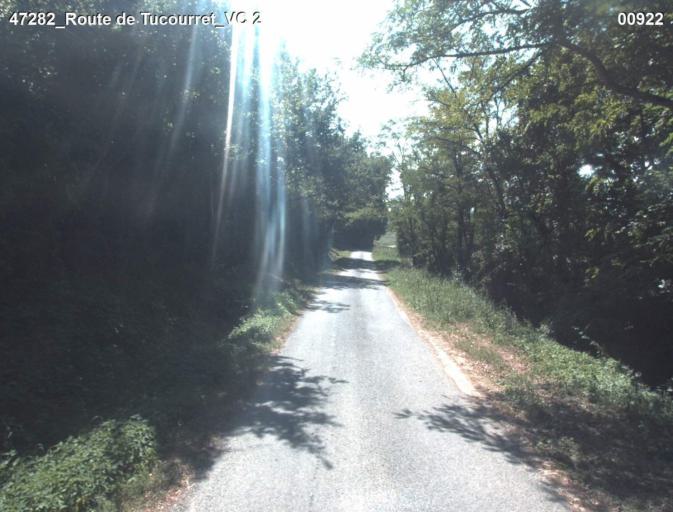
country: FR
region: Aquitaine
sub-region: Departement du Lot-et-Garonne
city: Laplume
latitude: 44.1020
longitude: 0.4824
